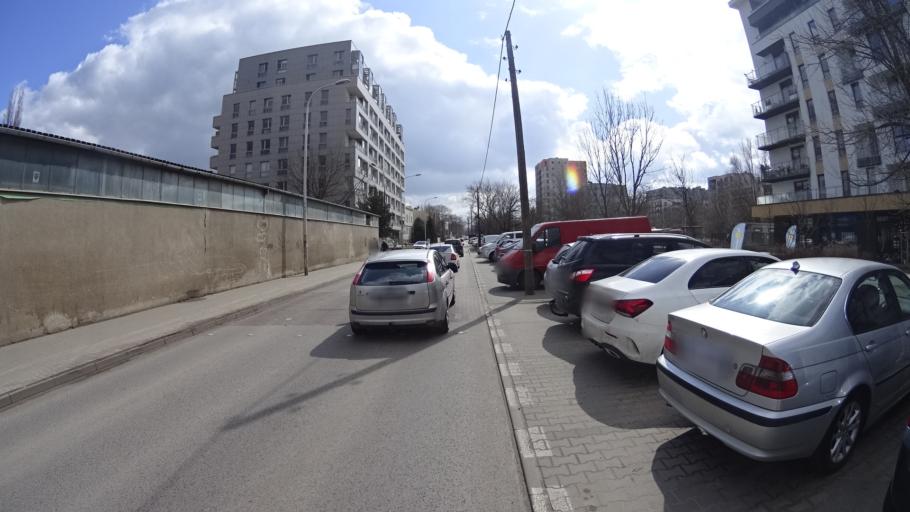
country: PL
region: Masovian Voivodeship
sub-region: Warszawa
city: Bemowo
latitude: 52.2238
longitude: 20.9366
